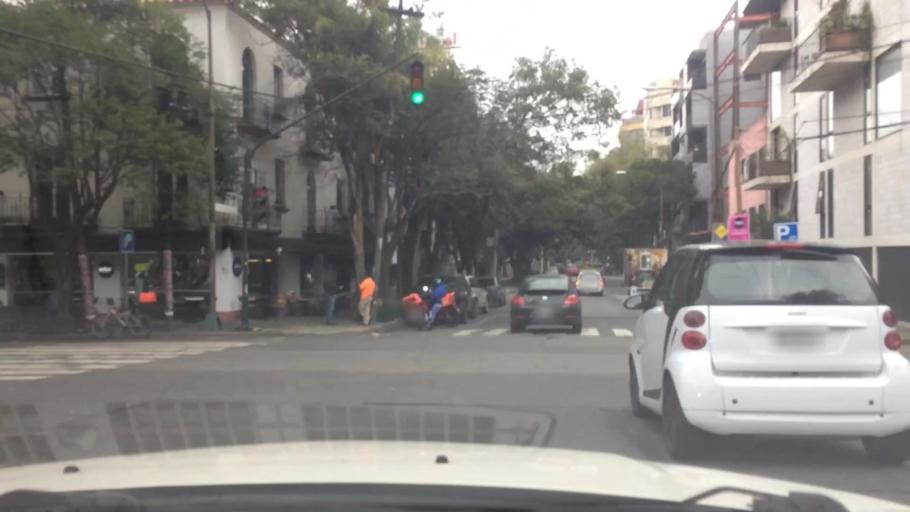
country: MX
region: Mexico City
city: Benito Juarez
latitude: 19.4075
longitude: -99.1745
